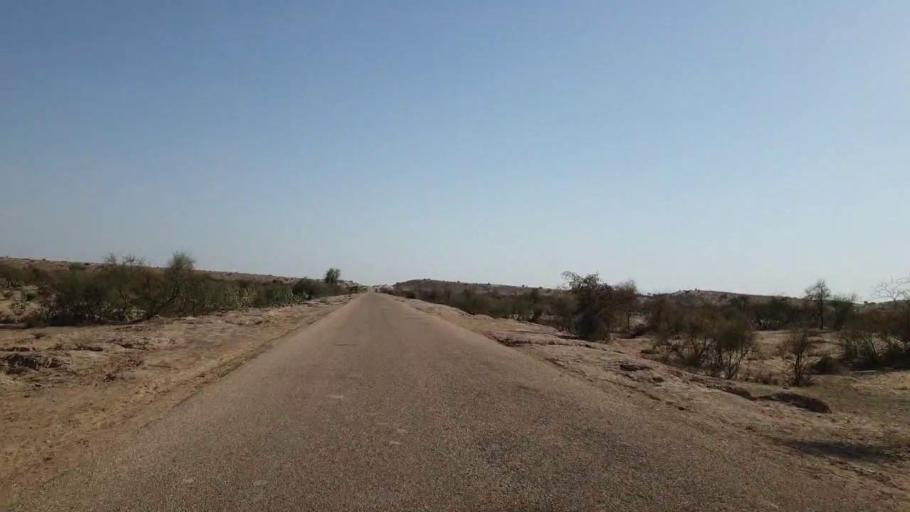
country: PK
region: Sindh
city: Nabisar
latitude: 25.0896
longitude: 70.0404
